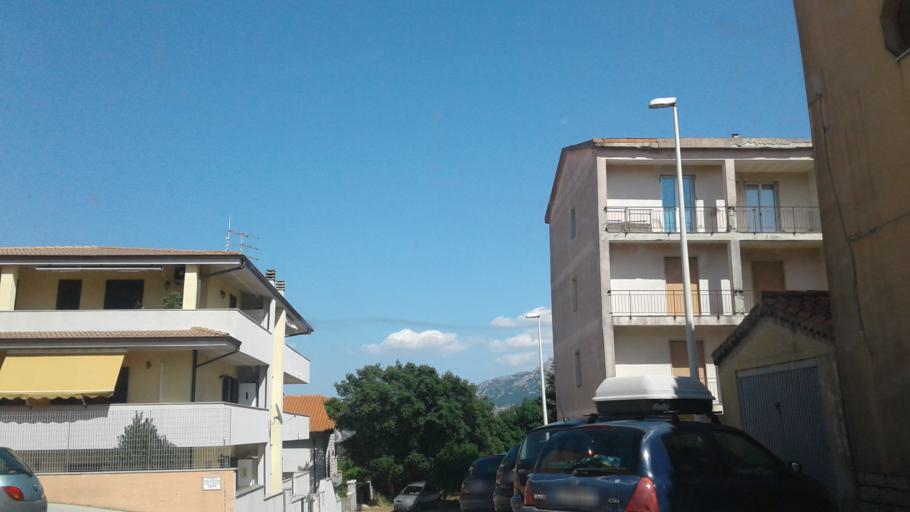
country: IT
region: Sardinia
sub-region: Provincia di Olbia-Tempio
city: Tempio Pausania
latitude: 40.8972
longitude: 9.1080
